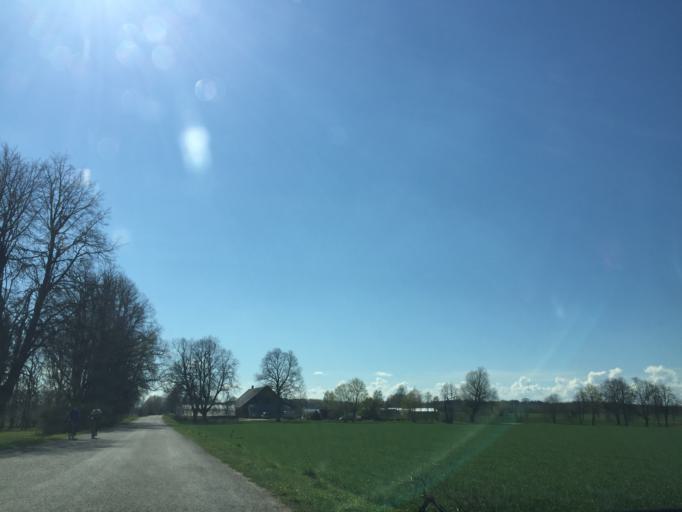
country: LV
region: Strenci
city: Strenci
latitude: 57.5392
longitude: 25.7025
